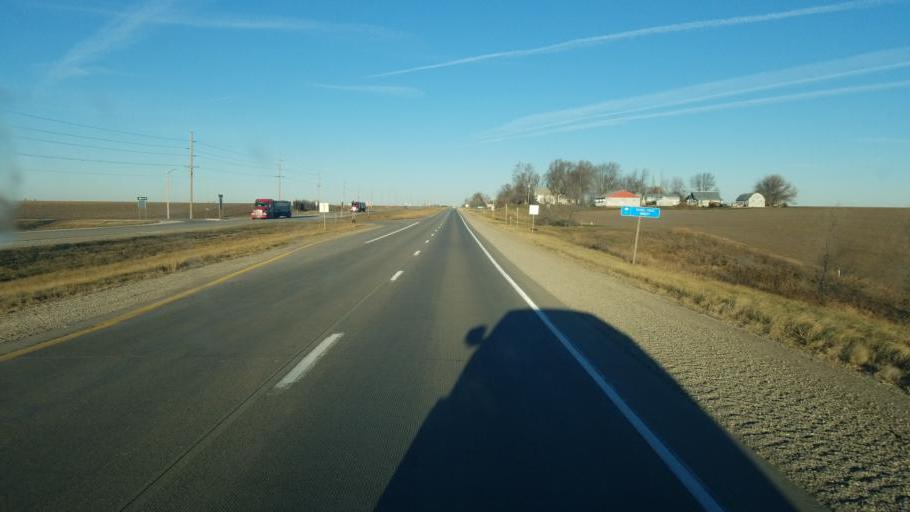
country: US
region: Iowa
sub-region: Mahaska County
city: Oskaloosa
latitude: 41.3358
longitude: -92.7287
